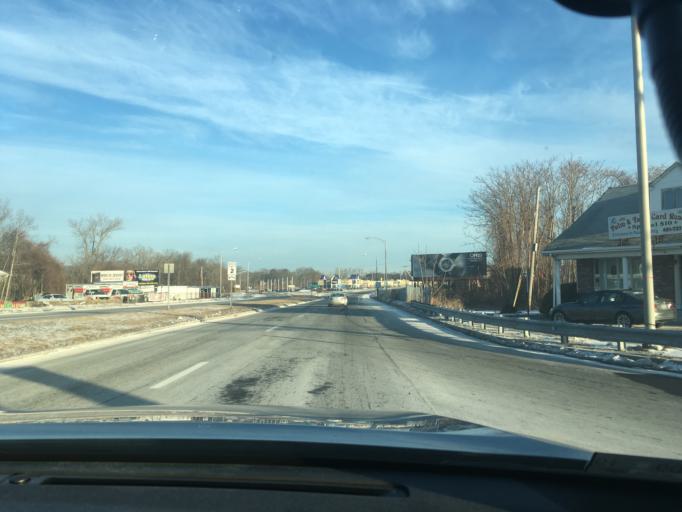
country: US
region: Rhode Island
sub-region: Kent County
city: West Warwick
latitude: 41.7277
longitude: -71.4801
